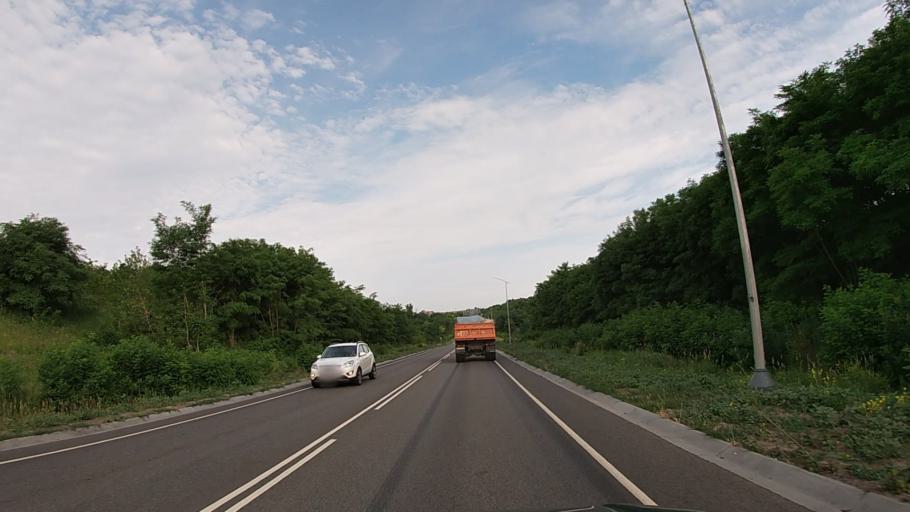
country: RU
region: Belgorod
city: Severnyy
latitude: 50.6672
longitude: 36.4934
